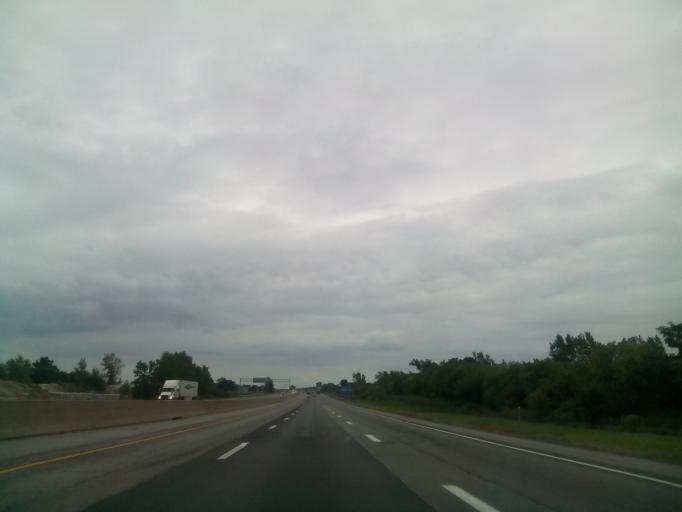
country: US
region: Ohio
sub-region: Huron County
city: Bellevue
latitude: 41.3436
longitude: -82.7806
